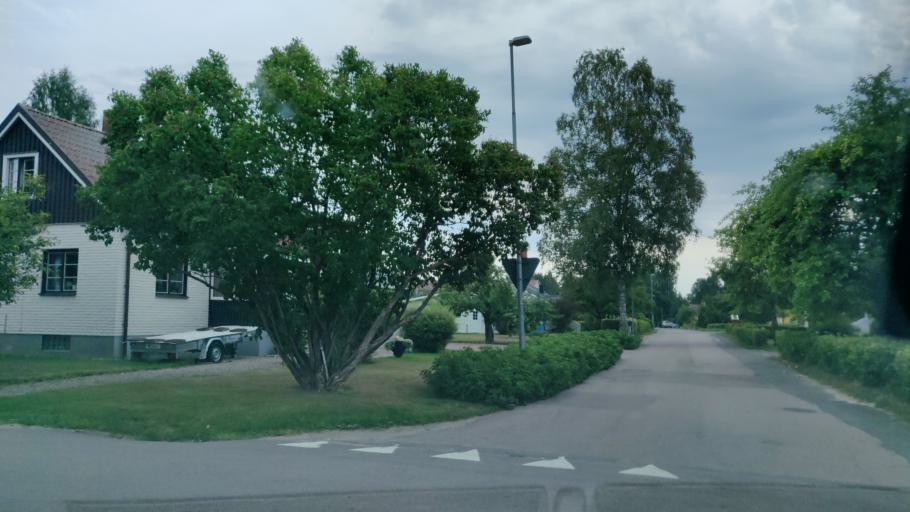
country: SE
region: Vaermland
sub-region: Munkfors Kommun
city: Munkfors
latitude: 59.8343
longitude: 13.5203
